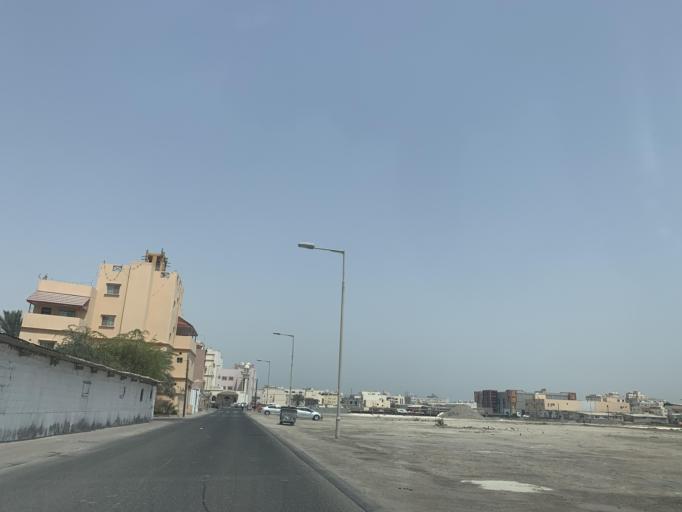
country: BH
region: Northern
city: Madinat `Isa
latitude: 26.1836
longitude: 50.5529
